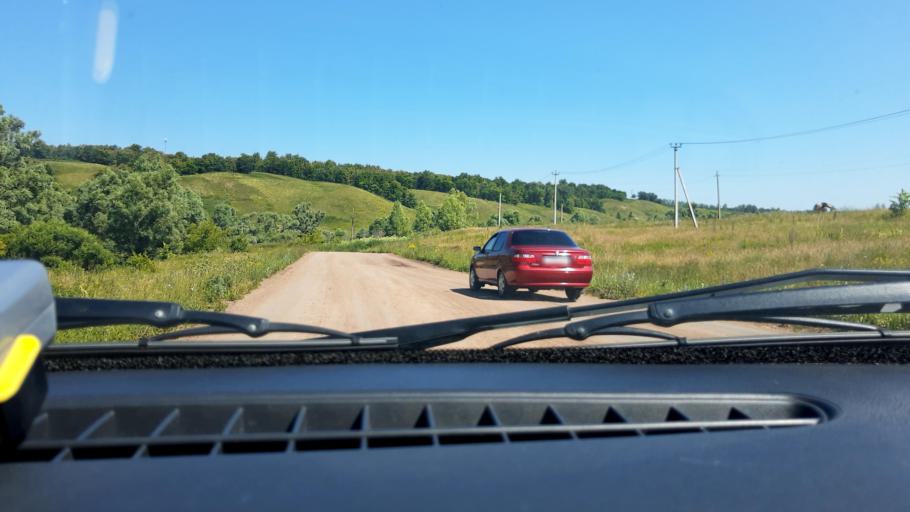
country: RU
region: Bashkortostan
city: Karmaskaly
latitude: 54.3574
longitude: 55.9028
